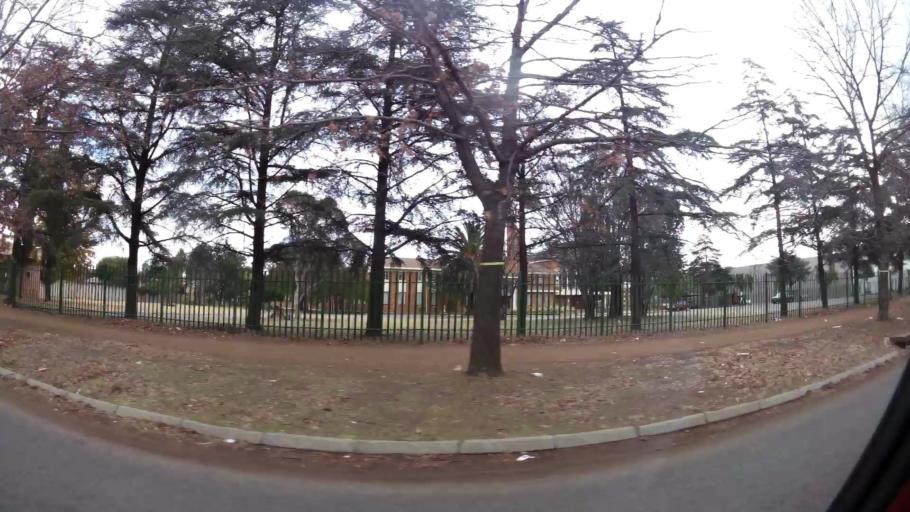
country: ZA
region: Gauteng
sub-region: Sedibeng District Municipality
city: Vanderbijlpark
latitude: -26.7111
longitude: 27.8252
